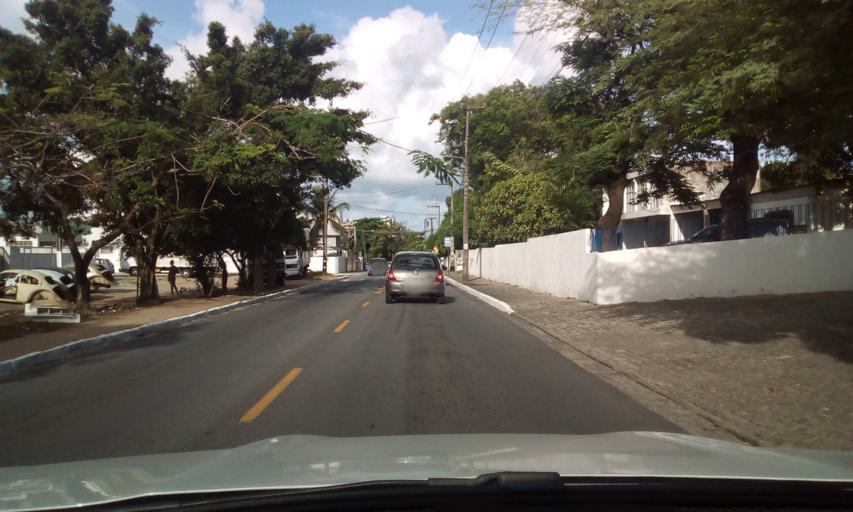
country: BR
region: Paraiba
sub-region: Joao Pessoa
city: Joao Pessoa
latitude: -7.1142
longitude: -34.8622
